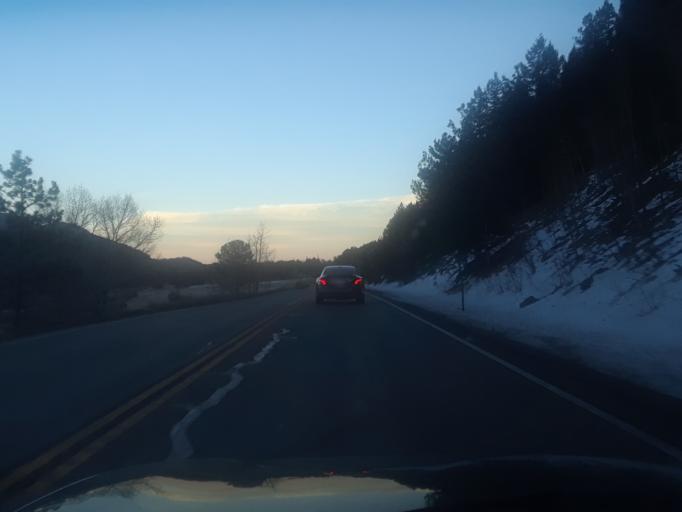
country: US
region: Colorado
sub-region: Clear Creek County
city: Georgetown
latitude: 39.4370
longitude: -105.5935
